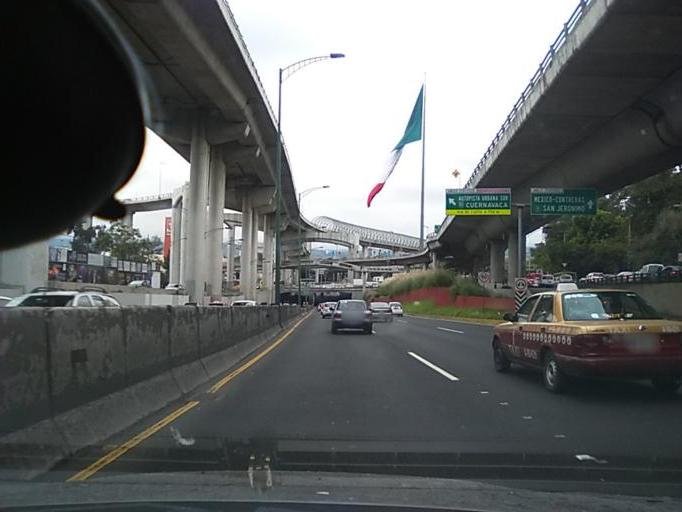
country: MX
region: Mexico City
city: Magdalena Contreras
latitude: 19.3332
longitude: -99.2094
